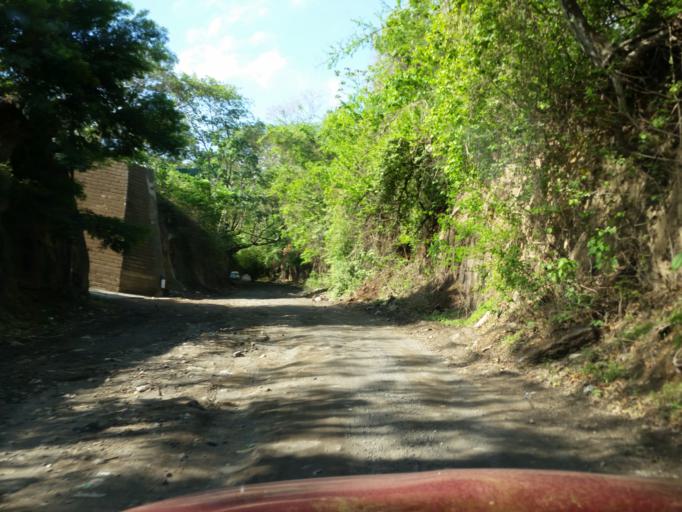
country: NI
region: Managua
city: Managua
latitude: 12.0899
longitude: -86.2623
